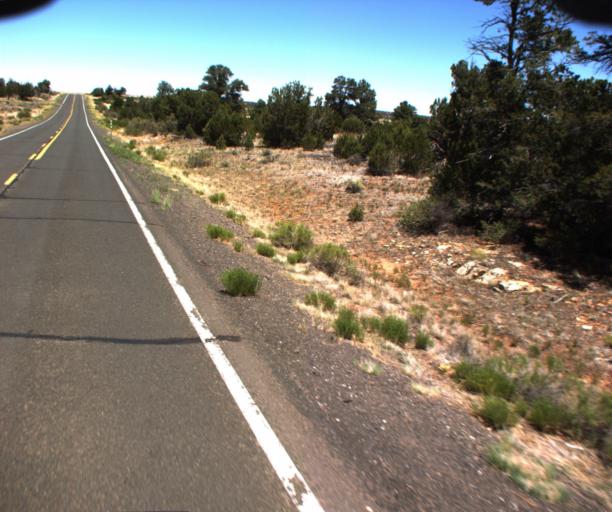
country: US
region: Arizona
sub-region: Coconino County
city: LeChee
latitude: 34.7162
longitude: -111.0911
